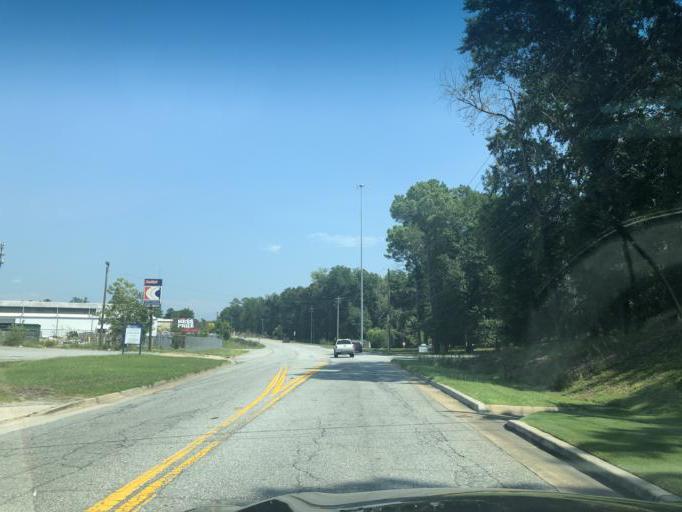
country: US
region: Georgia
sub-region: Muscogee County
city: Columbus
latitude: 32.5111
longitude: -84.9283
